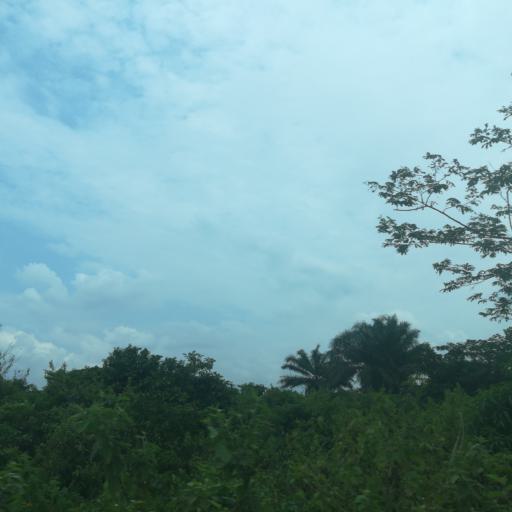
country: NG
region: Lagos
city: Ejirin
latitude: 6.6497
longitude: 3.8292
